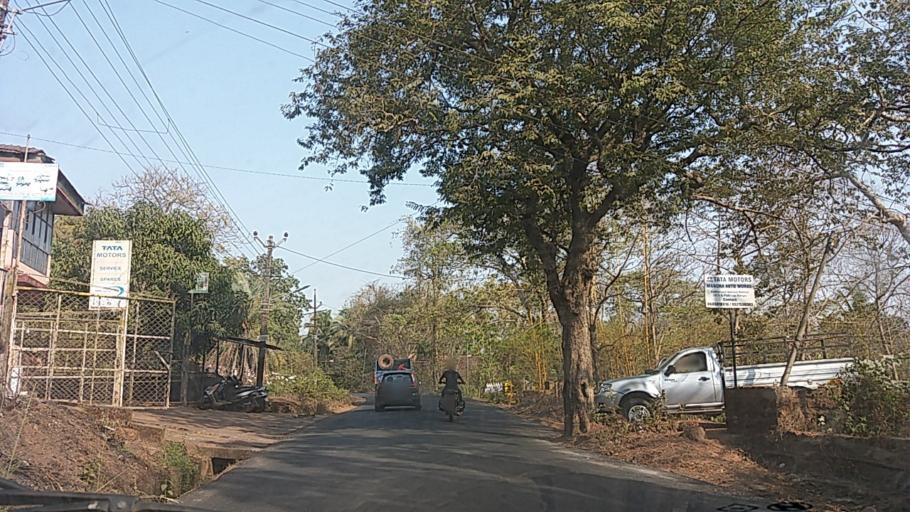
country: IN
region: Goa
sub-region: South Goa
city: Raia
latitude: 15.3079
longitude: 73.9673
